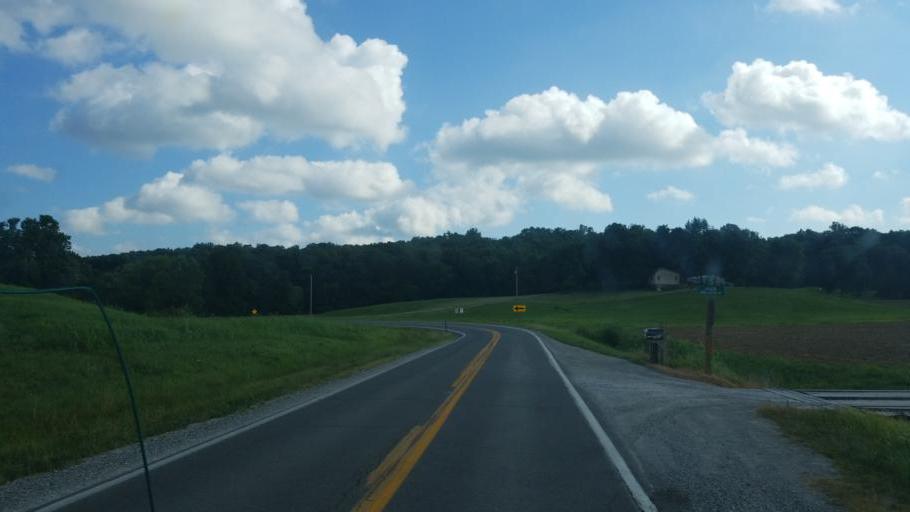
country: US
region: Illinois
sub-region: Union County
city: Cobden
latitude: 37.5480
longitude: -89.2659
